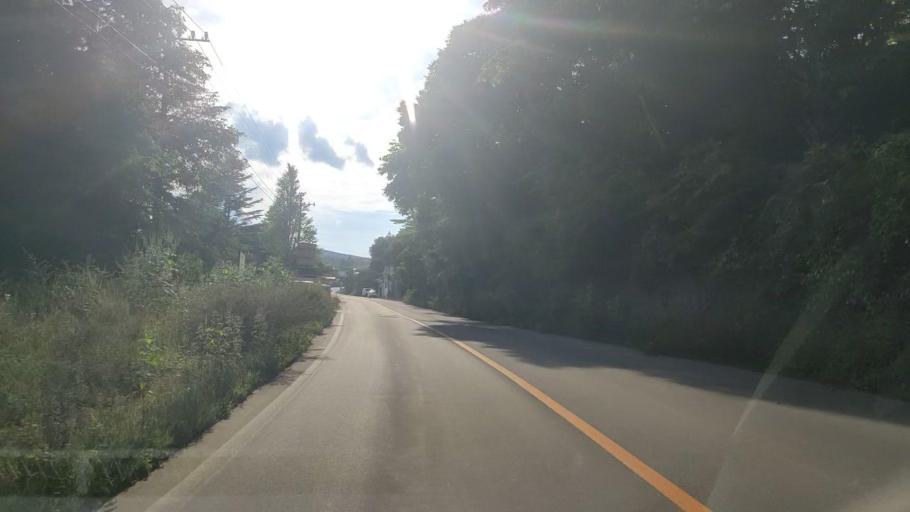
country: JP
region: Nagano
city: Komoro
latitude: 36.4875
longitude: 138.4371
